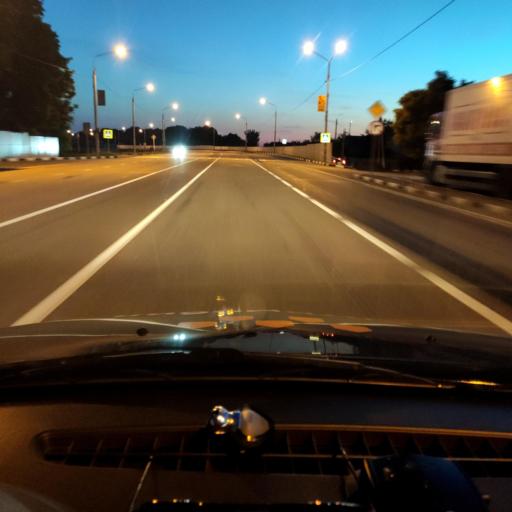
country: RU
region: Belgorod
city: Skorodnoye
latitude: 51.1868
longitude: 37.3690
